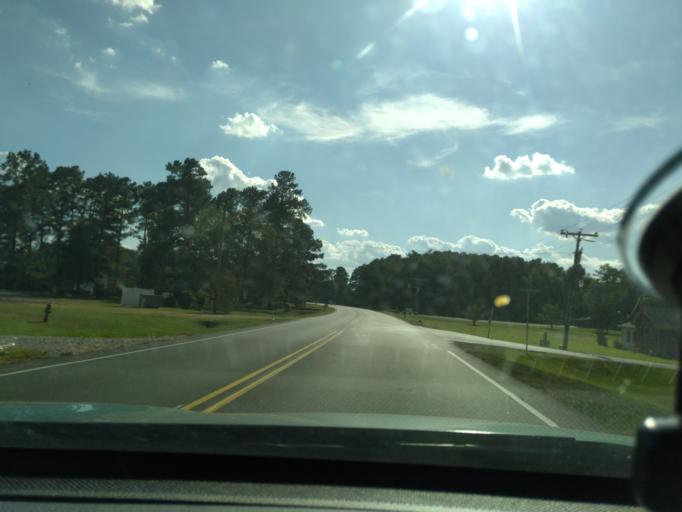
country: US
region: North Carolina
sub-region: Nash County
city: Sharpsburg
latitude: 35.9055
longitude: -77.8479
